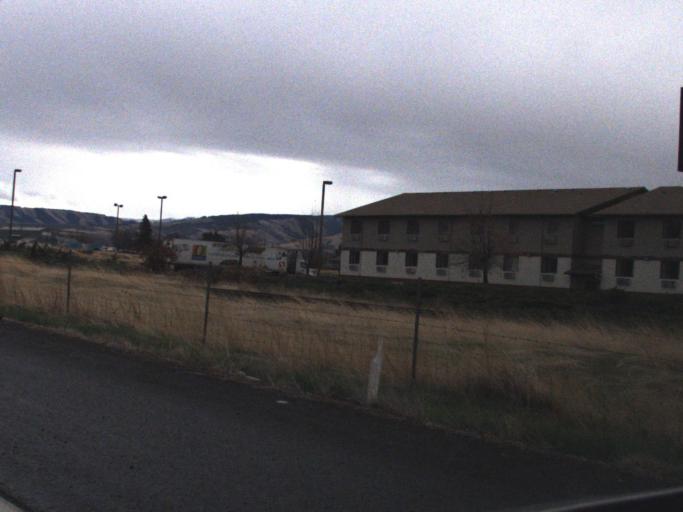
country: US
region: Washington
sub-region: Walla Walla County
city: Walla Walla East
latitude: 46.0811
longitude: -118.3030
